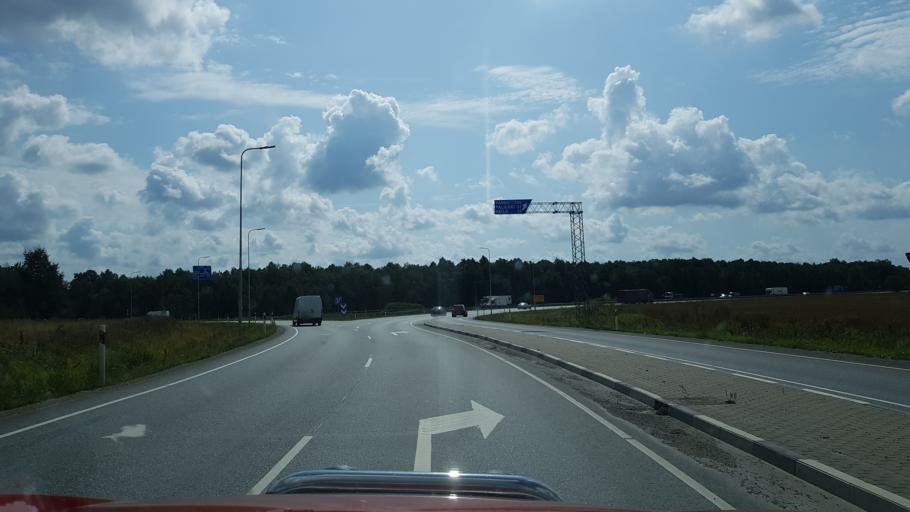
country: EE
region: Harju
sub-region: Rae vald
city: Jueri
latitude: 59.3540
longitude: 24.8786
